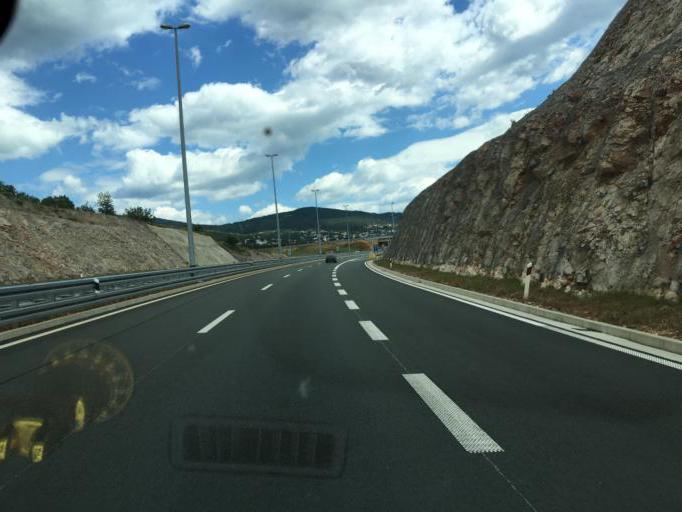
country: HR
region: Primorsko-Goranska
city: Hreljin
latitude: 45.2897
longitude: 14.5822
